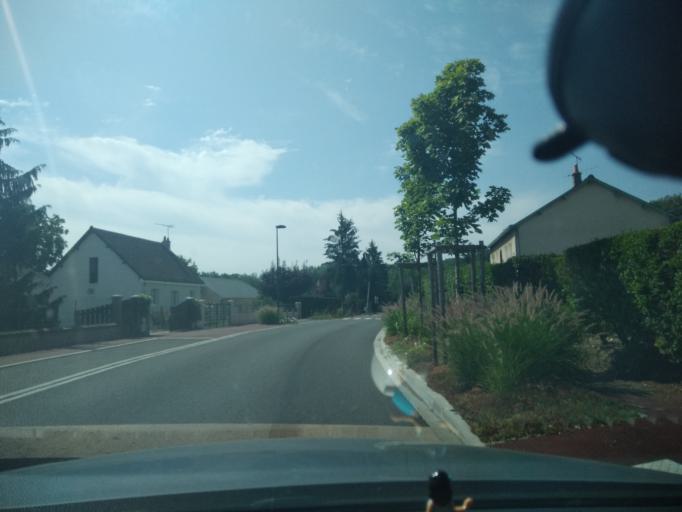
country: FR
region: Centre
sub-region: Departement d'Indre-et-Loire
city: Chambourg-sur-Indre
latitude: 47.1791
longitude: 0.9705
